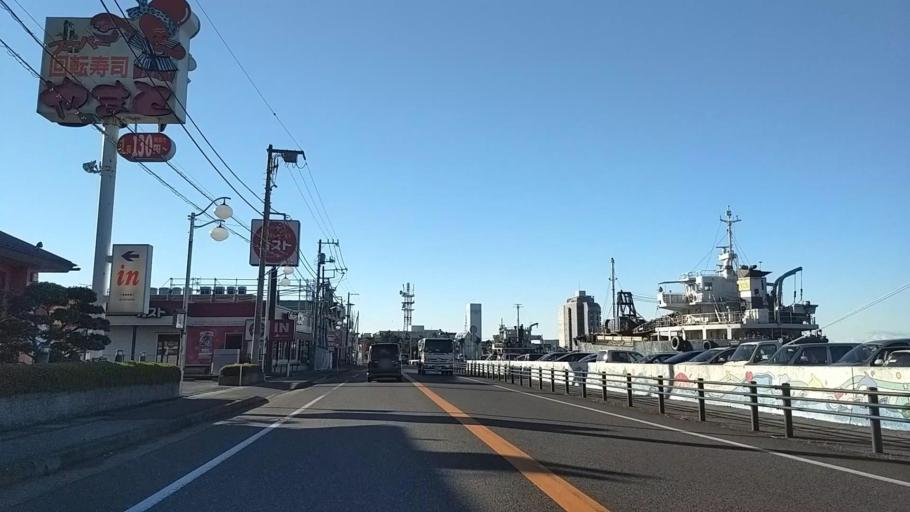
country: JP
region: Chiba
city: Kisarazu
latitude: 35.3845
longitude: 139.9181
